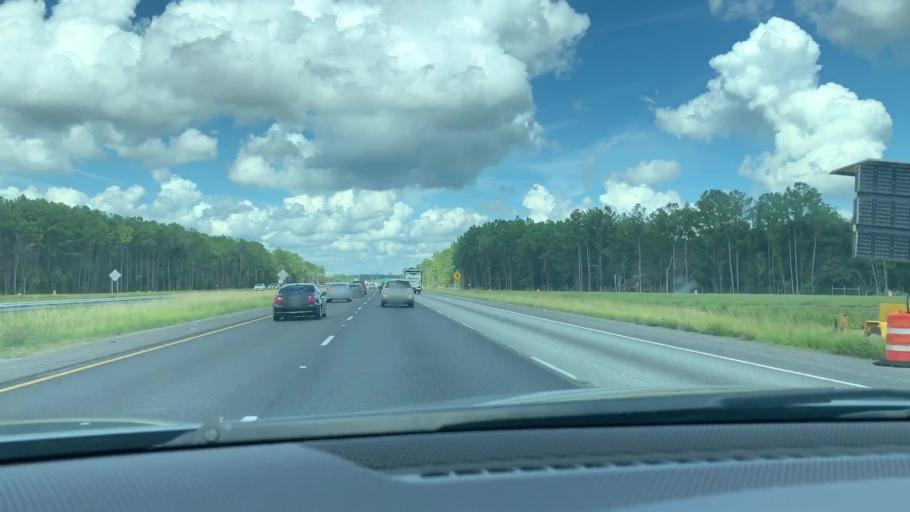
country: US
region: Georgia
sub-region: Camden County
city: Kingsland
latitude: 30.8268
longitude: -81.6667
